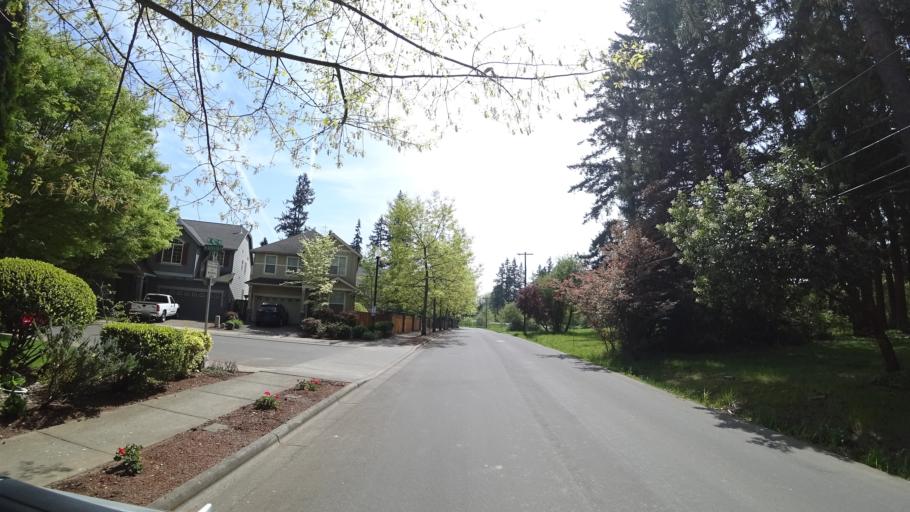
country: US
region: Oregon
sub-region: Washington County
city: Hillsboro
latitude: 45.5230
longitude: -122.9355
